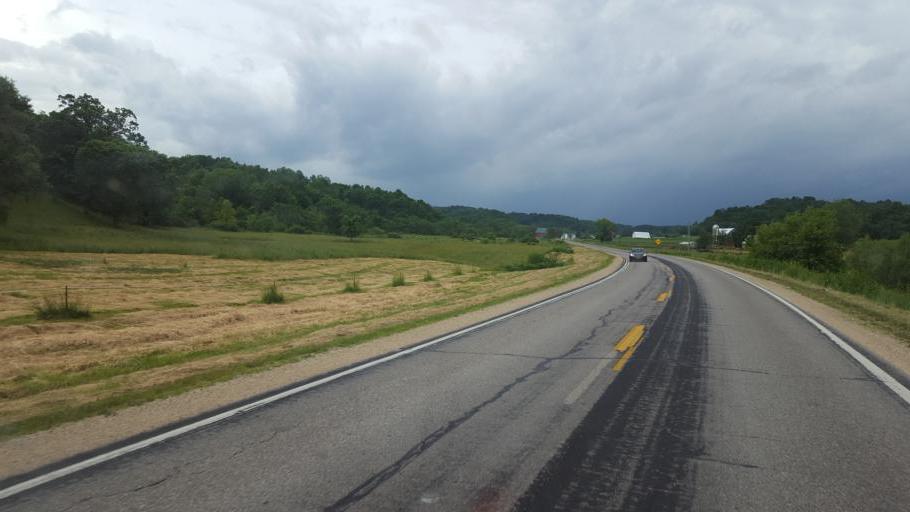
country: US
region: Wisconsin
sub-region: Vernon County
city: Hillsboro
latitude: 43.6535
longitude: -90.3951
